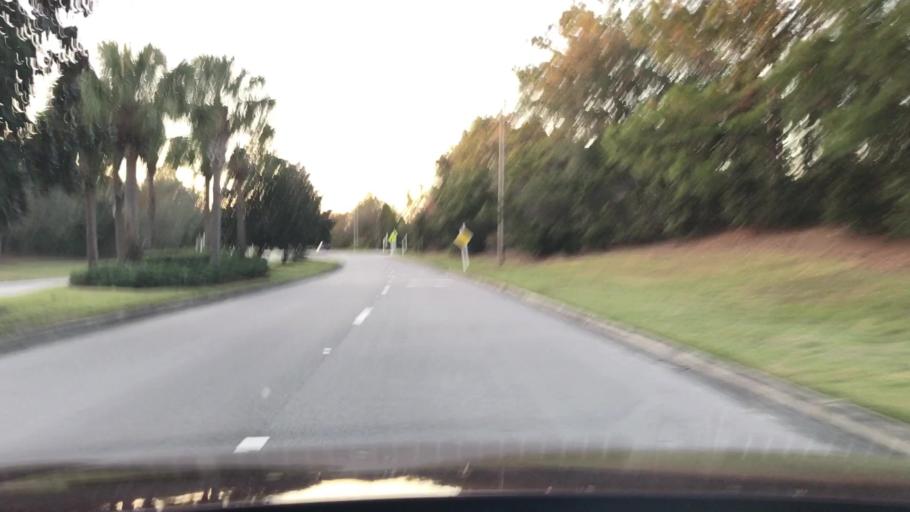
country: US
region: Florida
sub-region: Sarasota County
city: The Meadows
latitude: 27.4246
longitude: -82.3975
